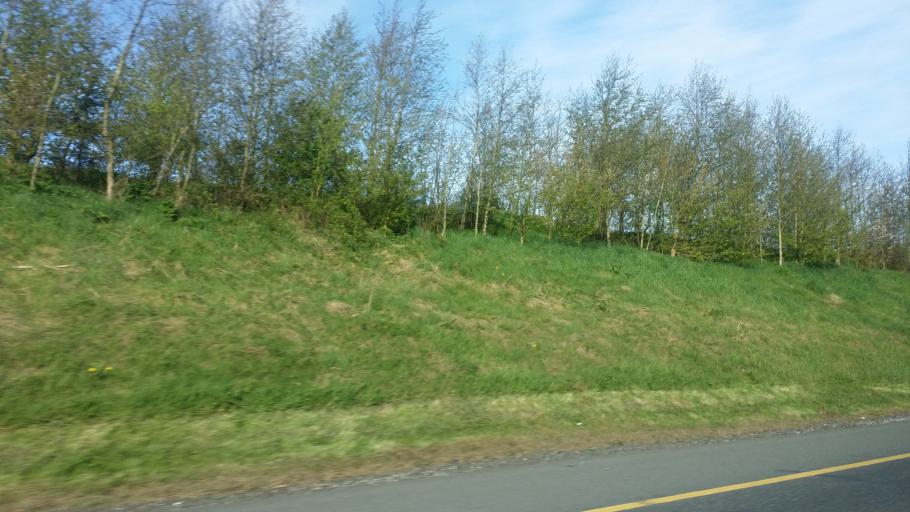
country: IE
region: Leinster
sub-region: An Mhi
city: Dunshaughlin
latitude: 53.5689
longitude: -6.5718
